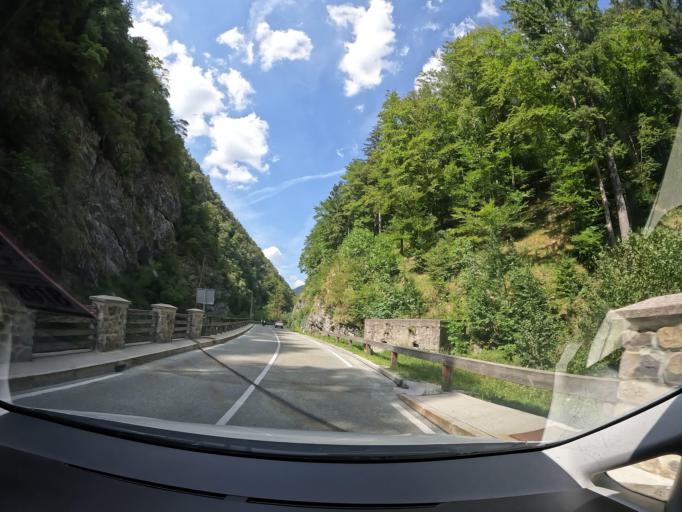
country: SI
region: Cerklje na Gorenjskem
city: Cerklje na Gorenjskem
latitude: 46.3122
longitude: 14.5006
